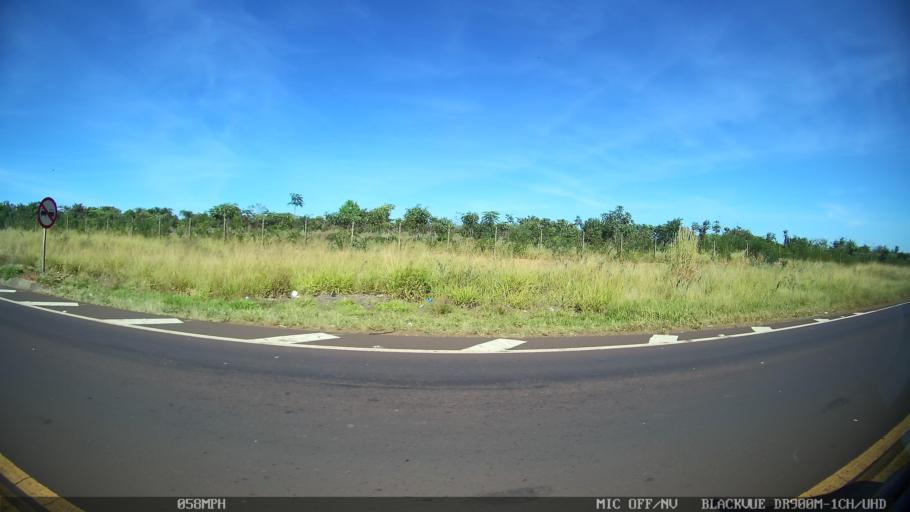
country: BR
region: Sao Paulo
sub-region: Franca
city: Franca
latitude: -20.5461
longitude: -47.4755
